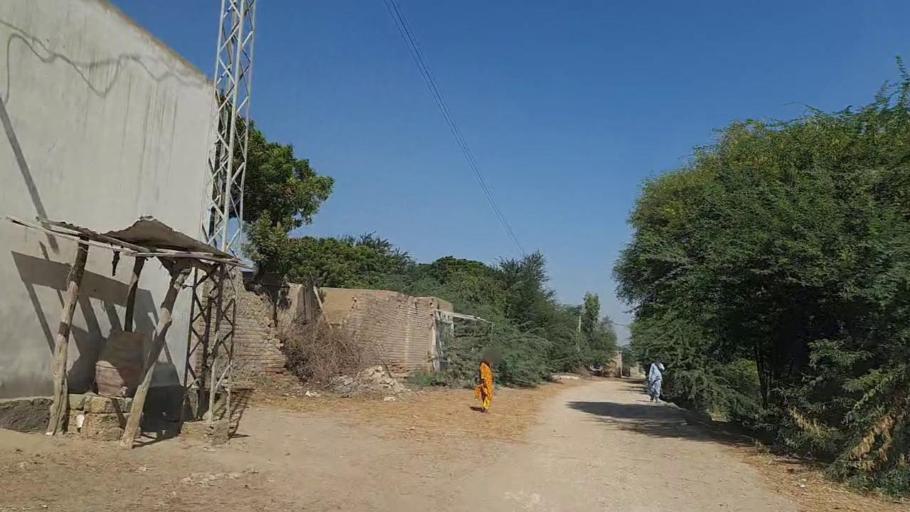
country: PK
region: Sindh
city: Daro Mehar
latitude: 24.7968
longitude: 68.1790
